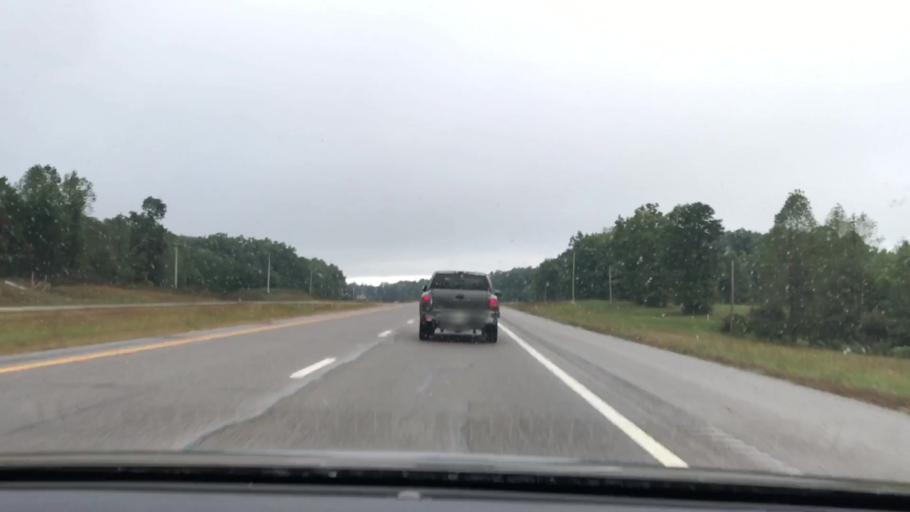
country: US
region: Tennessee
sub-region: Fentress County
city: Jamestown
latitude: 36.3645
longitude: -84.9461
